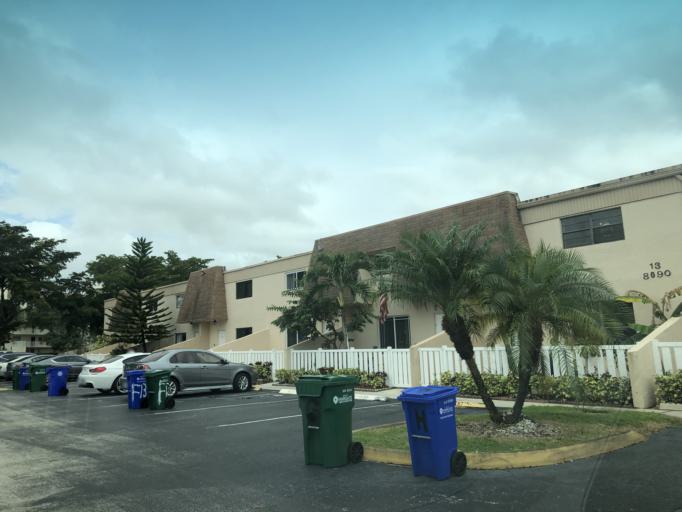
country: US
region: Florida
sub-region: Broward County
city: Margate
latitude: 26.2454
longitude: -80.2336
